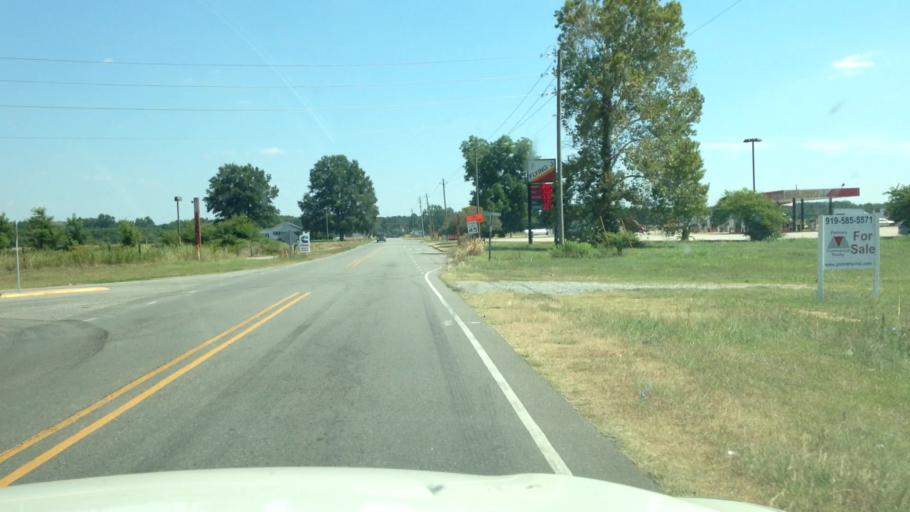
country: US
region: North Carolina
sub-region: Johnston County
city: Kenly
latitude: 35.5763
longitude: -78.1458
